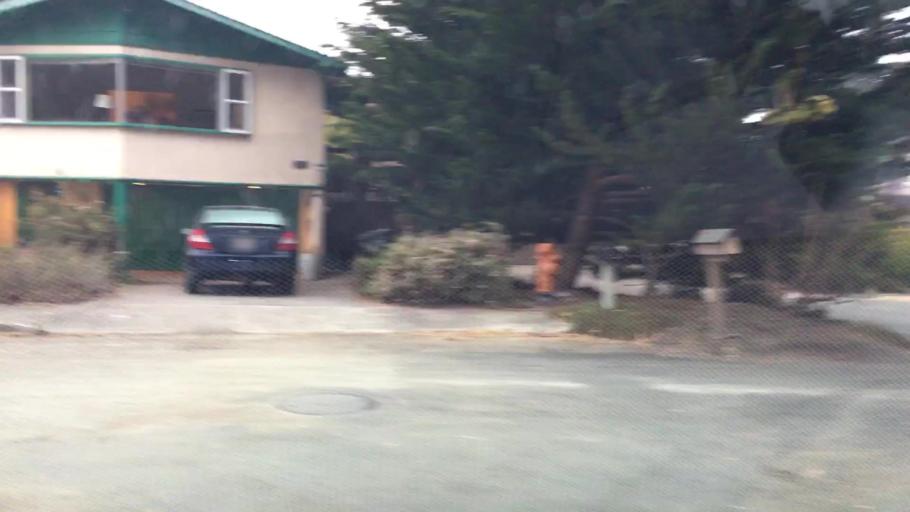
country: US
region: California
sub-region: San Mateo County
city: El Granada
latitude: 37.4946
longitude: -122.4560
